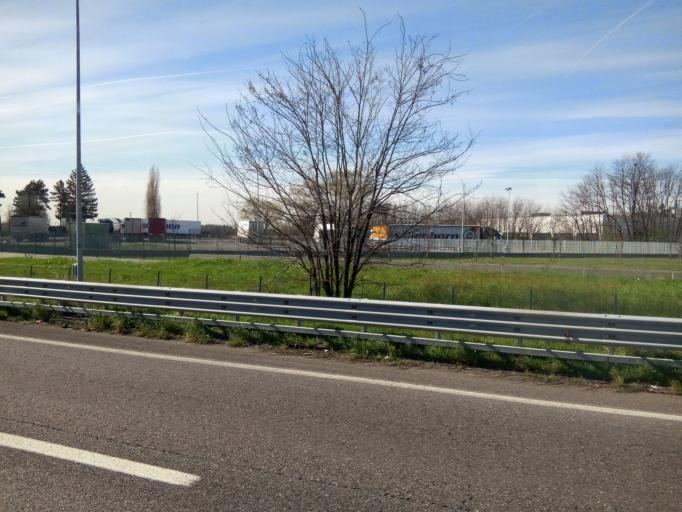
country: IT
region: Lombardy
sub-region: Citta metropolitana di Milano
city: Passirana
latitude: 45.5600
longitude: 9.0379
